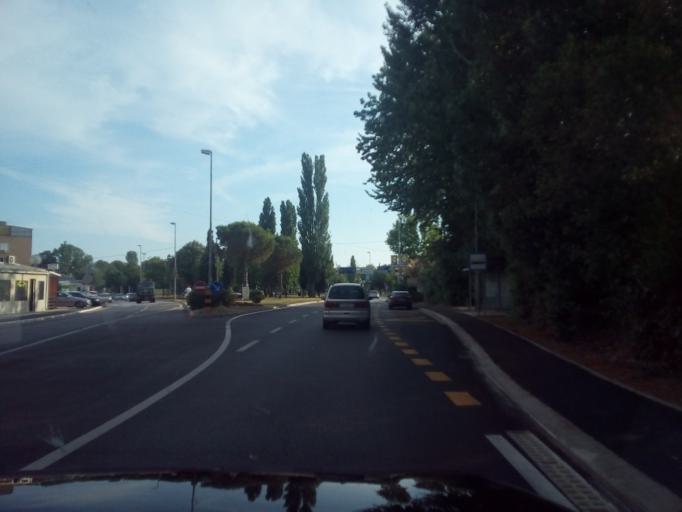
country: HR
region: Splitsko-Dalmatinska
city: Solin
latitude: 43.5363
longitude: 16.4867
